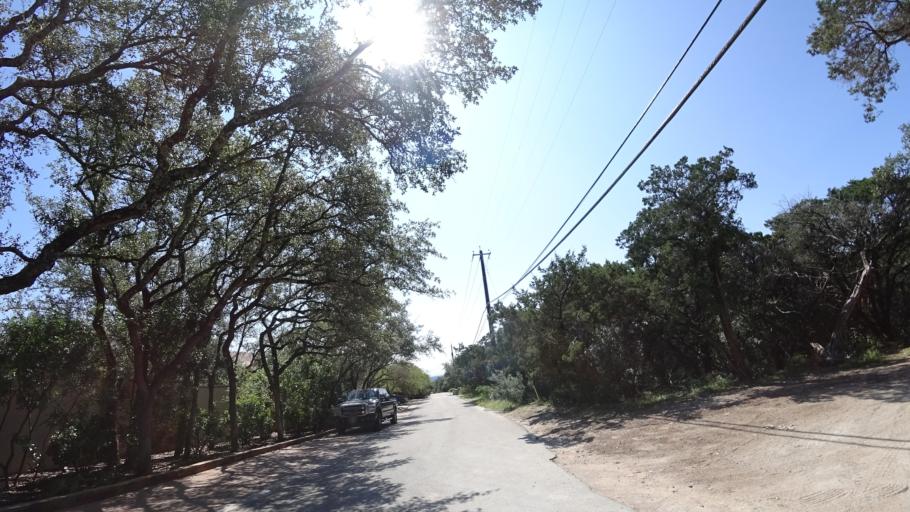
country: US
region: Texas
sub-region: Travis County
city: West Lake Hills
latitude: 30.3083
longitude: -97.7935
